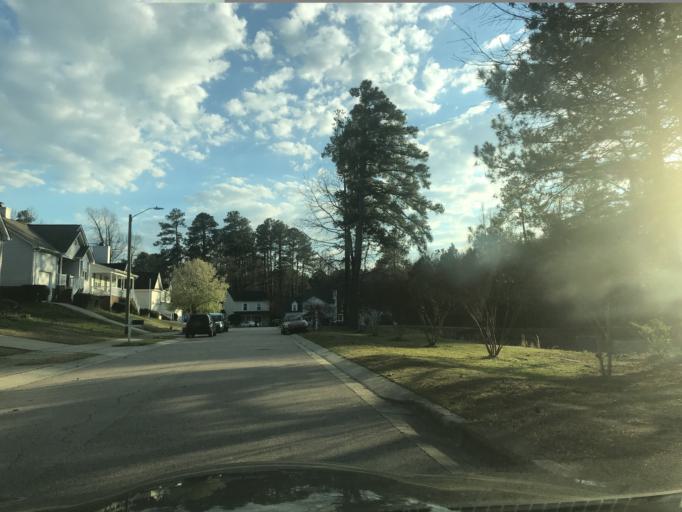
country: US
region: North Carolina
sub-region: Wake County
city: Raleigh
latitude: 35.8525
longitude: -78.5679
